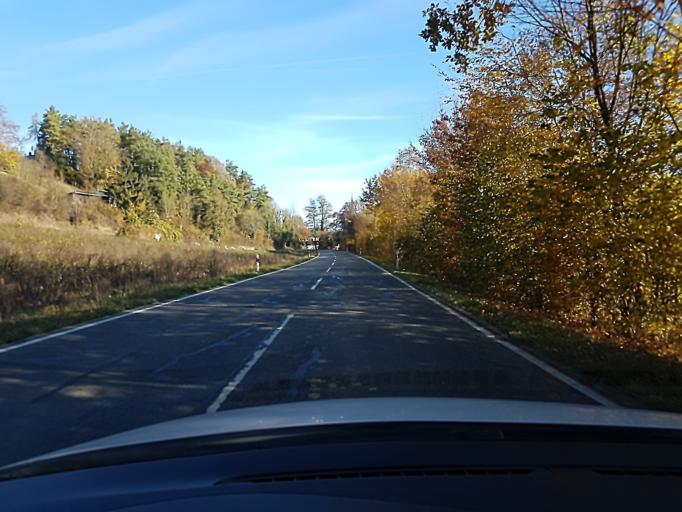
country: DE
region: Baden-Wuerttemberg
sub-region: Karlsruhe Region
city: Billigheim
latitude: 49.3446
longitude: 9.2525
